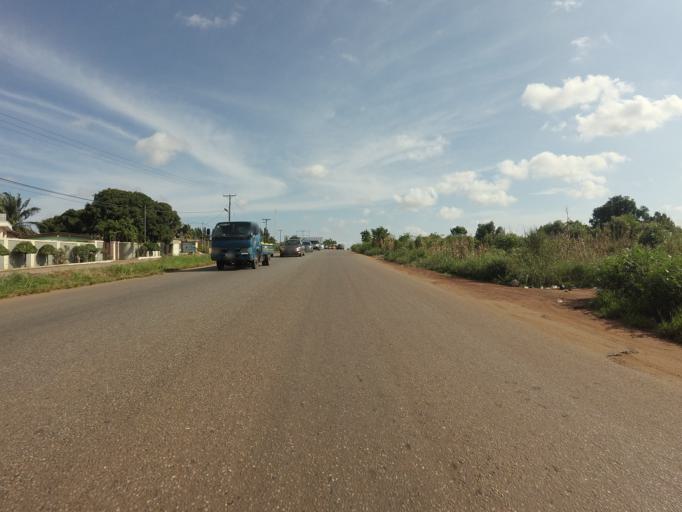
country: GH
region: Greater Accra
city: Medina Estates
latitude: 5.6496
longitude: -0.1693
